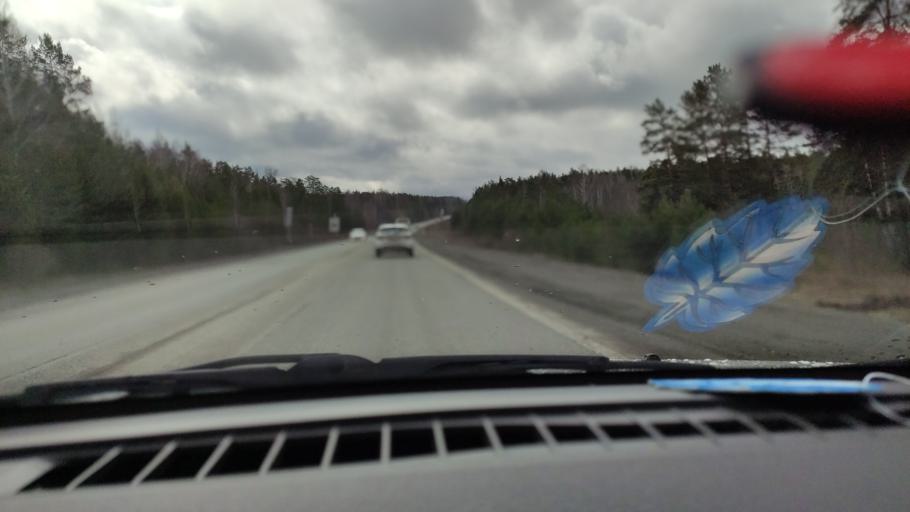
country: RU
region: Sverdlovsk
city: Talitsa
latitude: 56.8641
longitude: 60.0490
